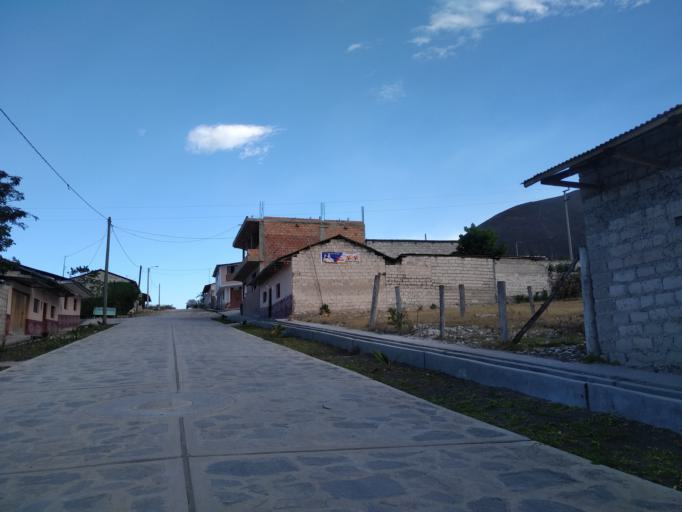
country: PE
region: Amazonas
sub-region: Provincia de Luya
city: Tingo
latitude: -6.3743
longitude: -77.9104
